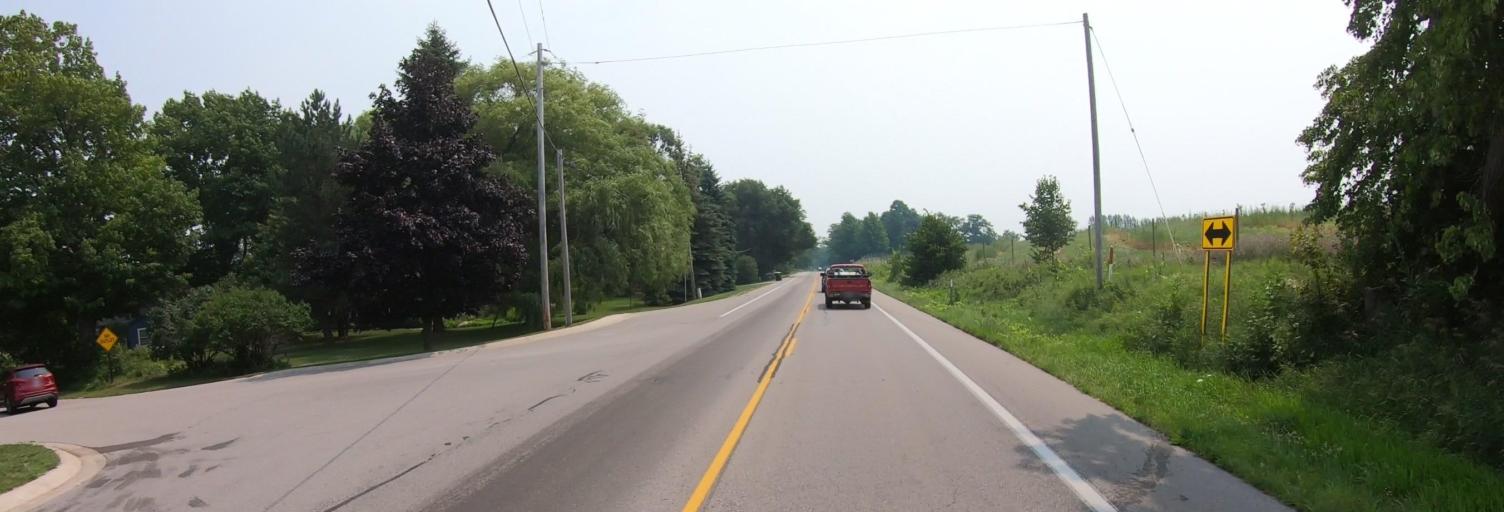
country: US
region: Michigan
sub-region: Leelanau County
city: Leland
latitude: 45.1029
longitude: -85.6126
